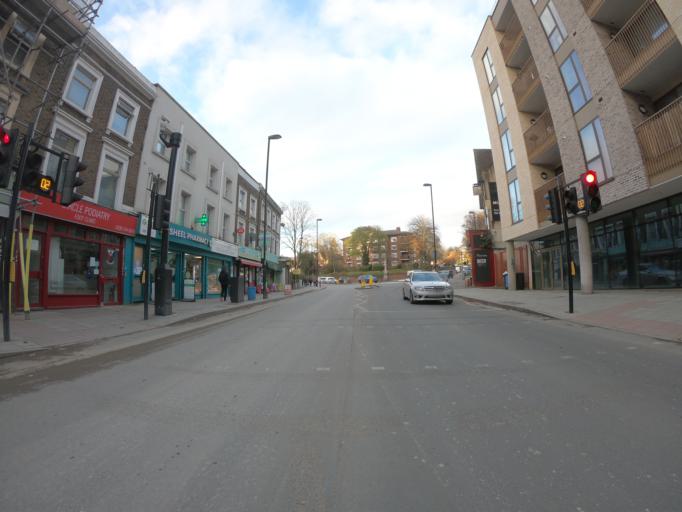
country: GB
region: England
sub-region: Greater London
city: Blackheath
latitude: 51.4655
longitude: -0.0111
